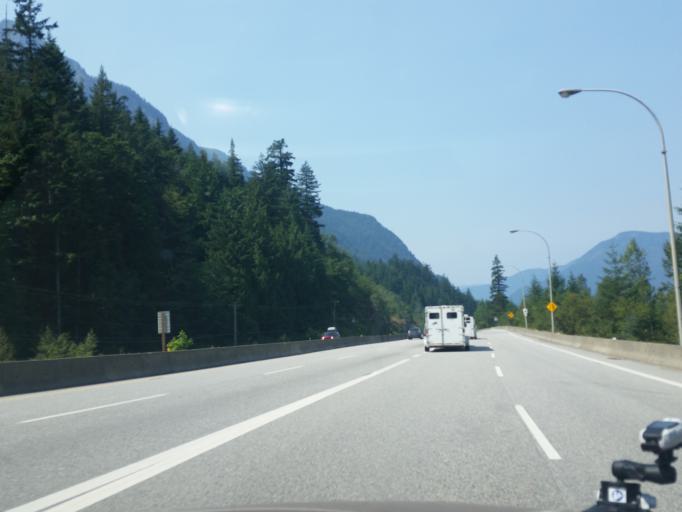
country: CA
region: British Columbia
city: Hope
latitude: 49.3622
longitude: -121.3677
